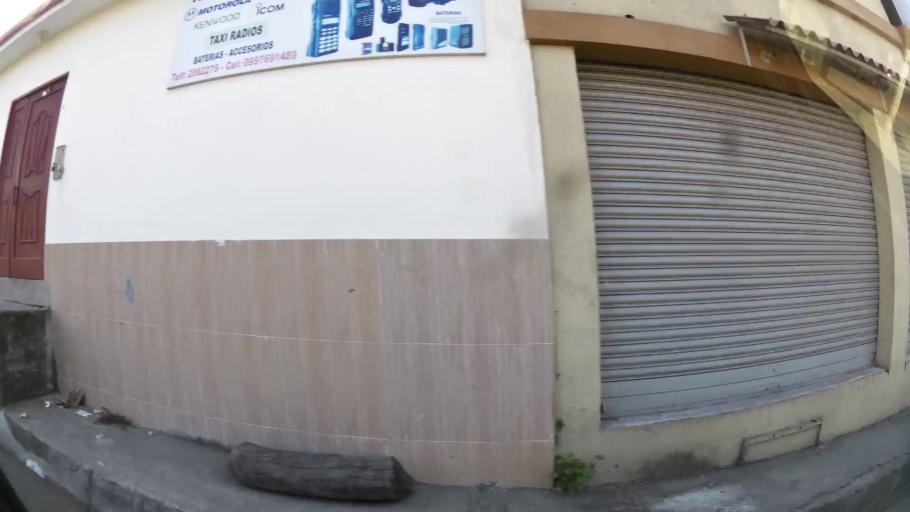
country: EC
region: Guayas
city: Guayaquil
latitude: -2.1572
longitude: -79.9125
